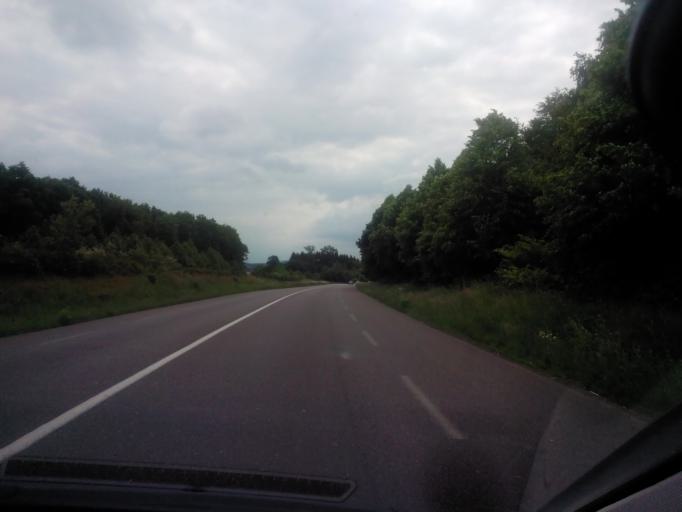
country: FR
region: Lorraine
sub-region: Departement de la Moselle
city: Carling
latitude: 49.1828
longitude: 6.7123
